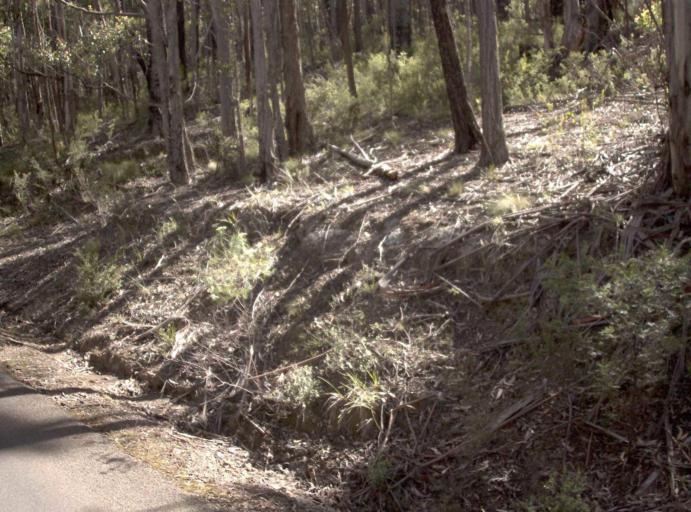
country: AU
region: Victoria
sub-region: East Gippsland
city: Lakes Entrance
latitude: -37.4410
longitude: 148.1316
